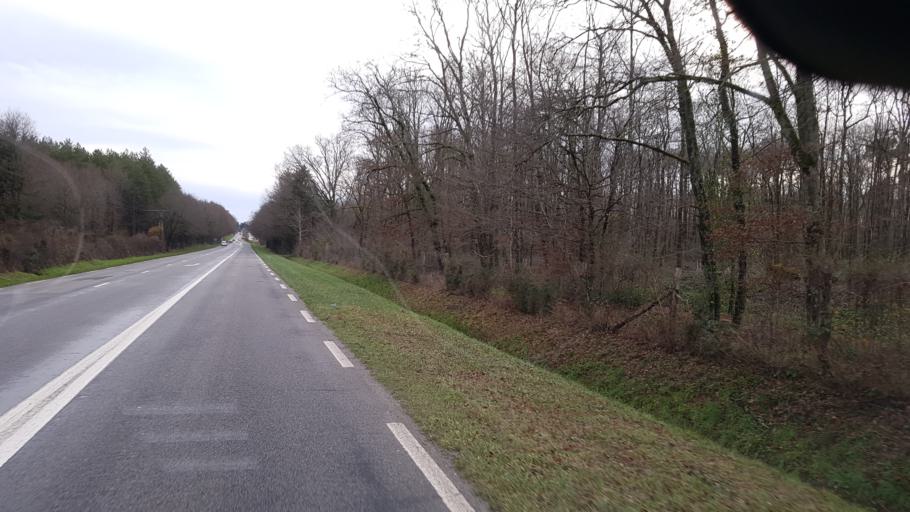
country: FR
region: Centre
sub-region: Departement du Loir-et-Cher
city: Nouan-le-Fuzelier
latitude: 47.5514
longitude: 2.0343
